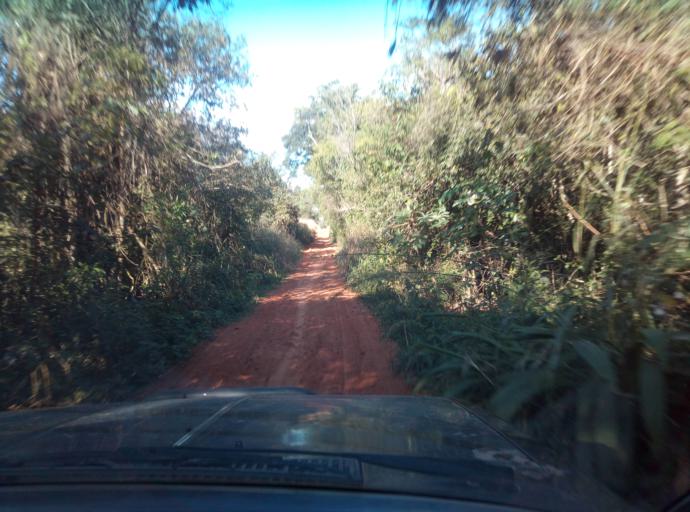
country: PY
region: Caaguazu
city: Carayao
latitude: -25.1738
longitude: -56.2765
